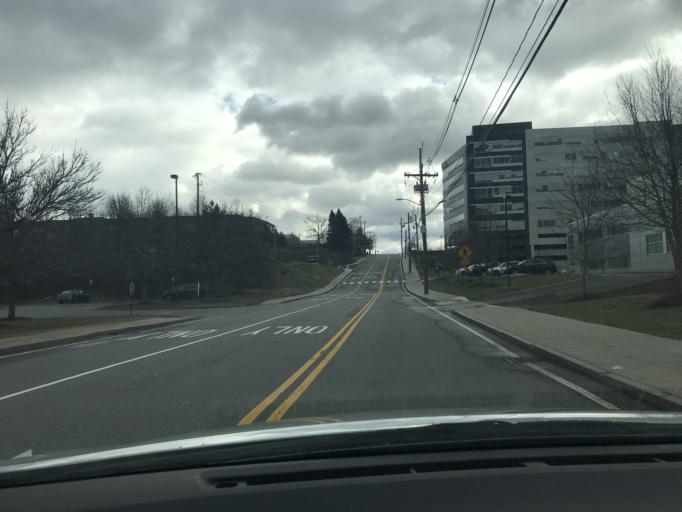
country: US
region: Massachusetts
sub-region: Middlesex County
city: Burlington
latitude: 42.4835
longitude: -71.2215
